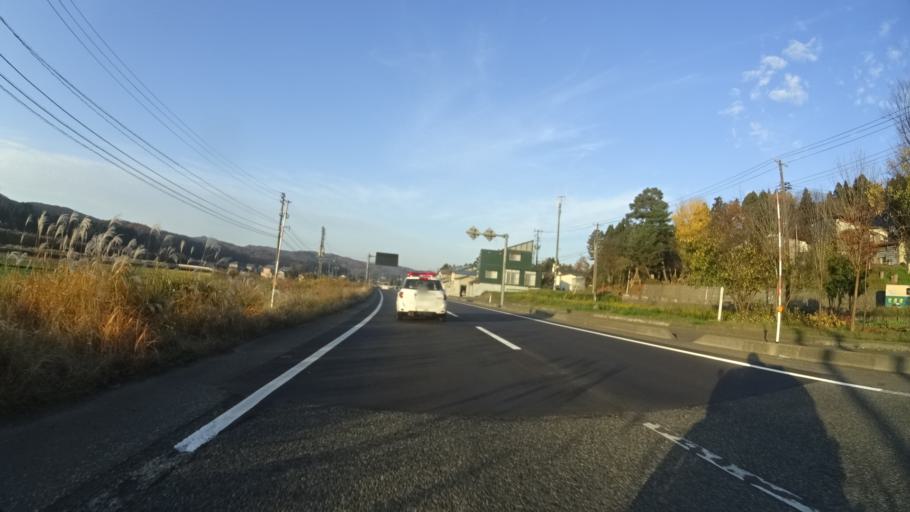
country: JP
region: Niigata
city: Nagaoka
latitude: 37.4424
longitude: 138.7424
